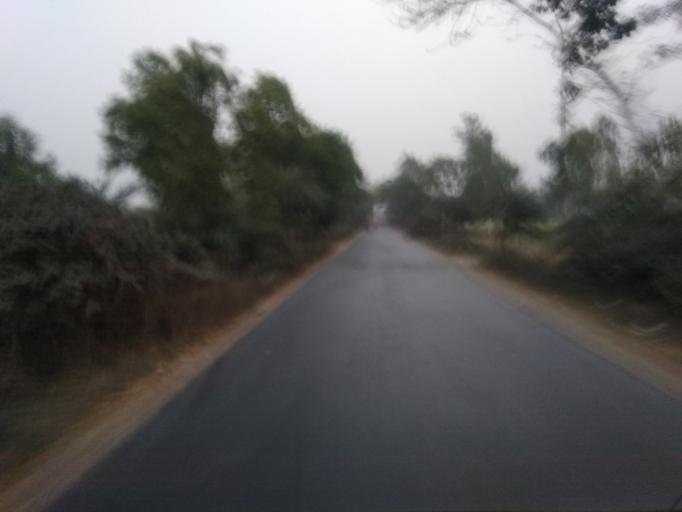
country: BD
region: Rajshahi
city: Bogra
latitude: 24.7351
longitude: 89.3280
